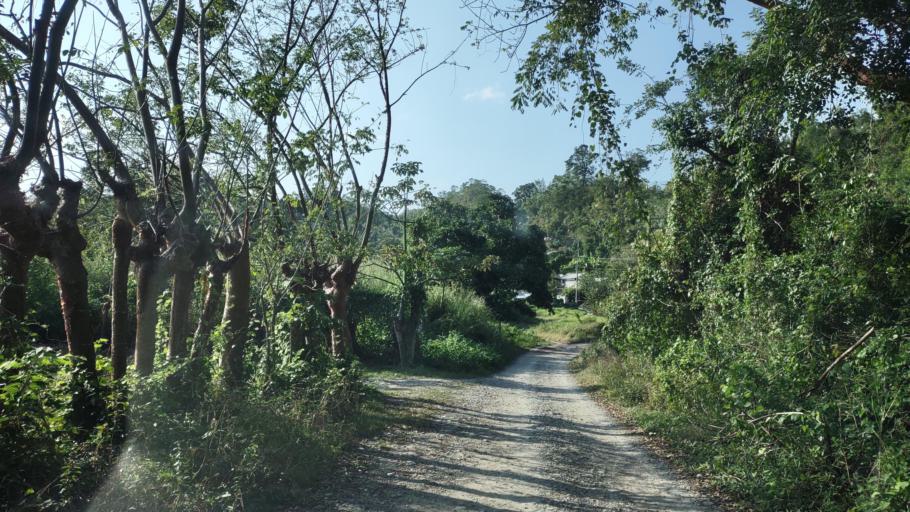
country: MX
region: Veracruz
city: Papantla de Olarte
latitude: 20.4604
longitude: -97.3612
